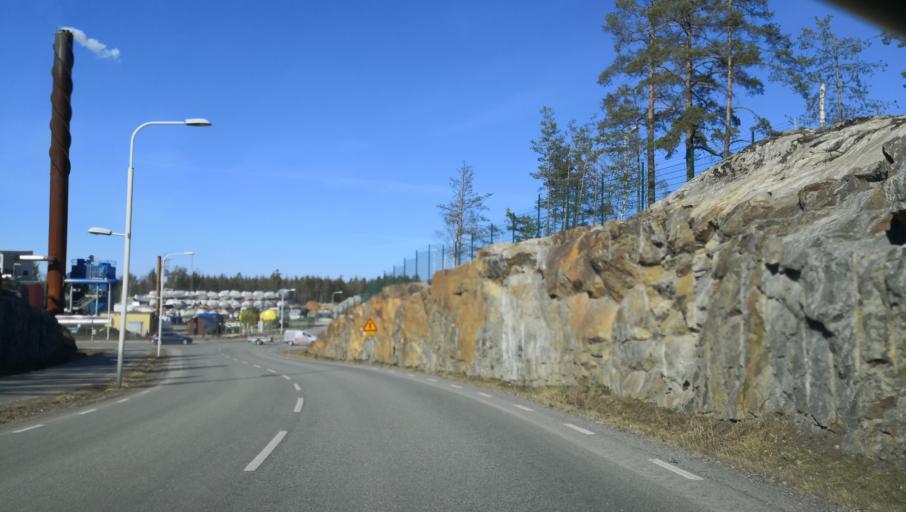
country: SE
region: Stockholm
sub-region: Varmdo Kommun
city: Gustavsberg
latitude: 59.3119
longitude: 18.3791
